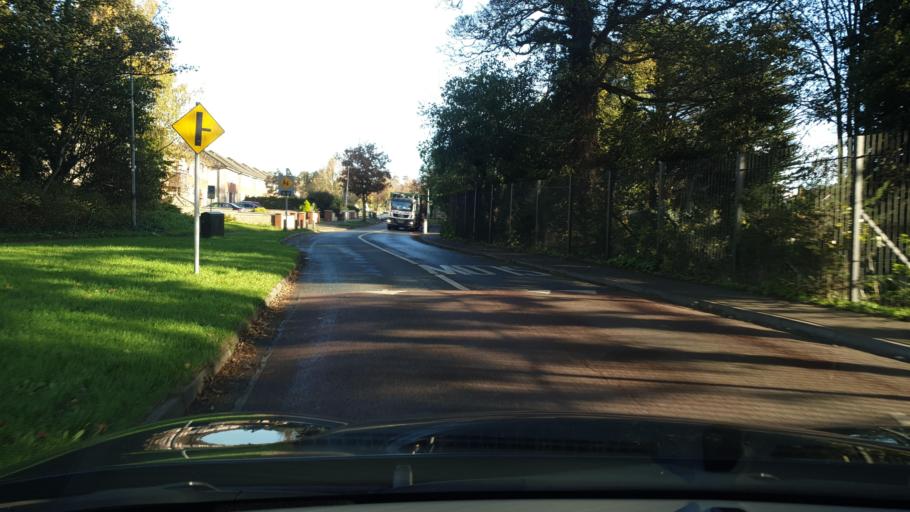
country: IE
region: Leinster
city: Lucan
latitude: 53.3512
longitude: -6.4360
